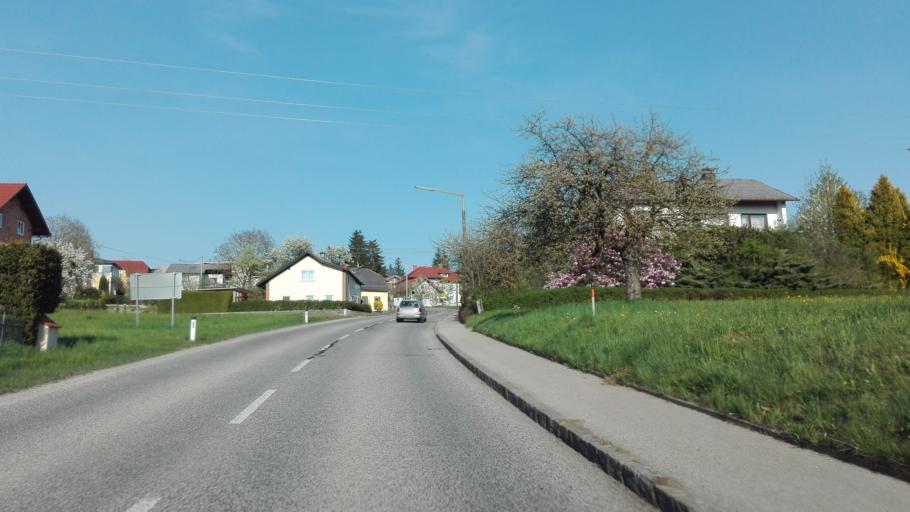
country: AT
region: Upper Austria
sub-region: Politischer Bezirk Grieskirchen
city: Grieskirchen
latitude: 48.3444
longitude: 13.7782
